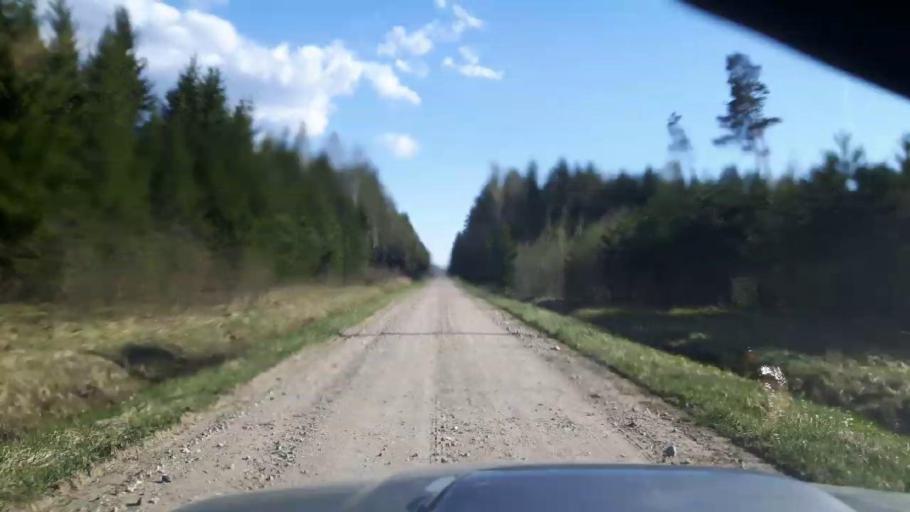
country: EE
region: Paernumaa
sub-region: Tootsi vald
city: Tootsi
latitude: 58.4259
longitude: 24.8515
